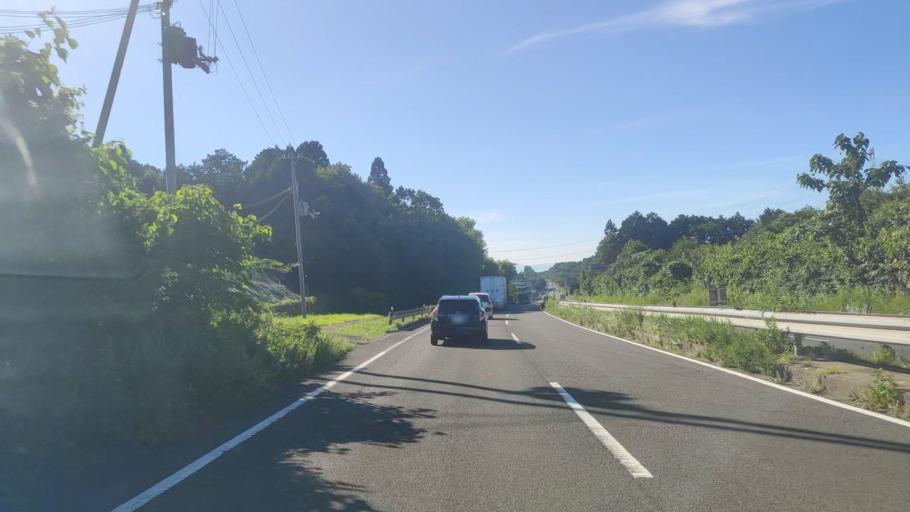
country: JP
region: Shiga Prefecture
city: Minakuchicho-matoba
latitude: 34.9623
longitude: 136.1999
